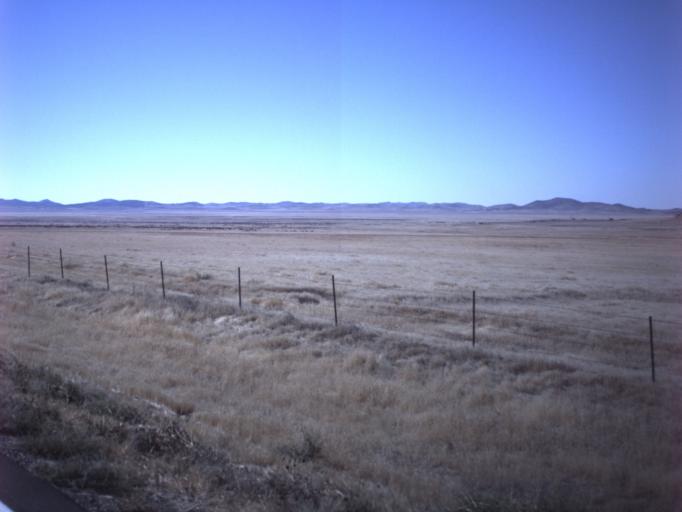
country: US
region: Utah
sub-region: Tooele County
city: Grantsville
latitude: 40.3875
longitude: -112.7473
